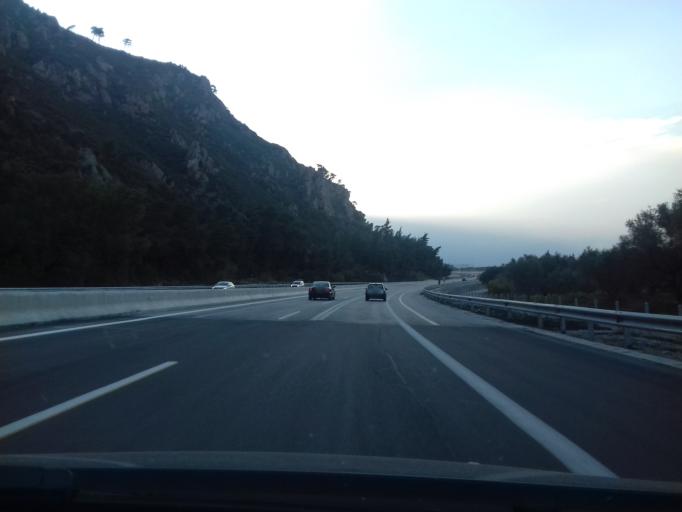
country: GR
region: West Greece
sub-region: Nomos Achaias
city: Temeni
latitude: 38.1866
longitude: 22.1785
